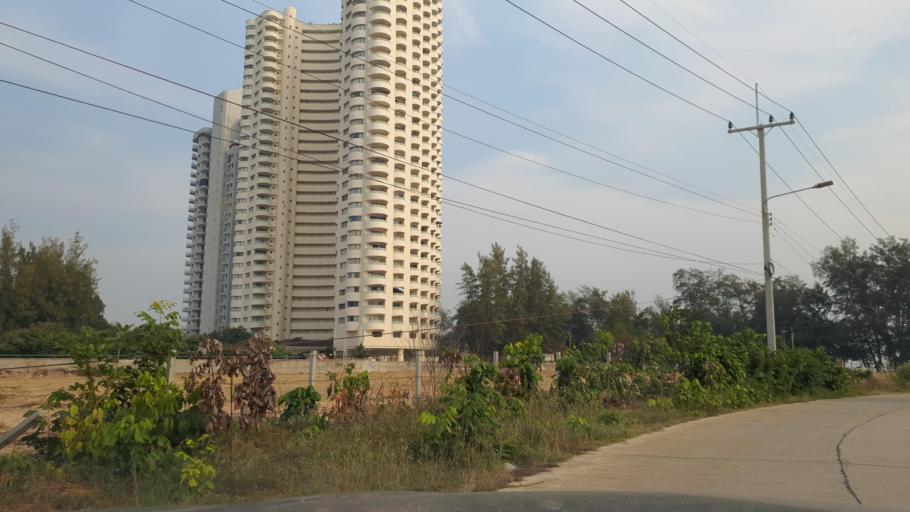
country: TH
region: Rayong
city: Rayong
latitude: 12.6050
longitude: 101.3994
